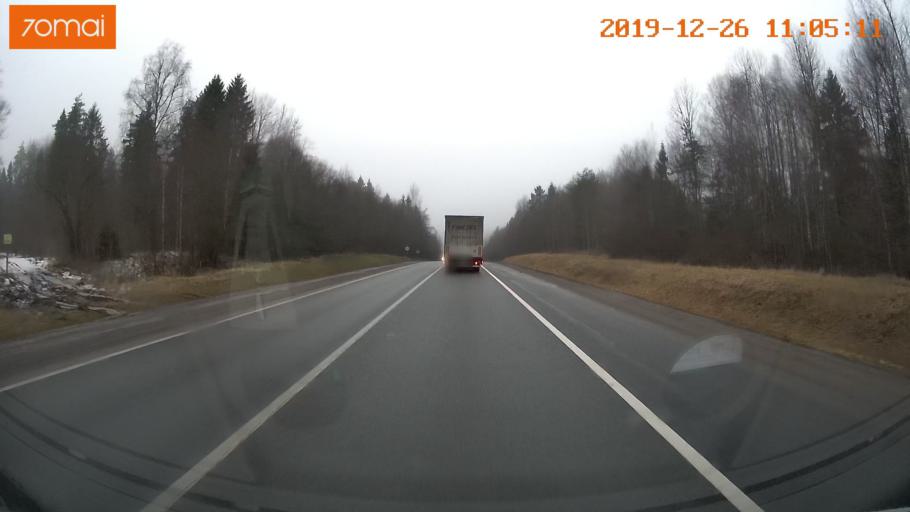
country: RU
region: Vologda
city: Molochnoye
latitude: 59.1462
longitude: 39.3506
